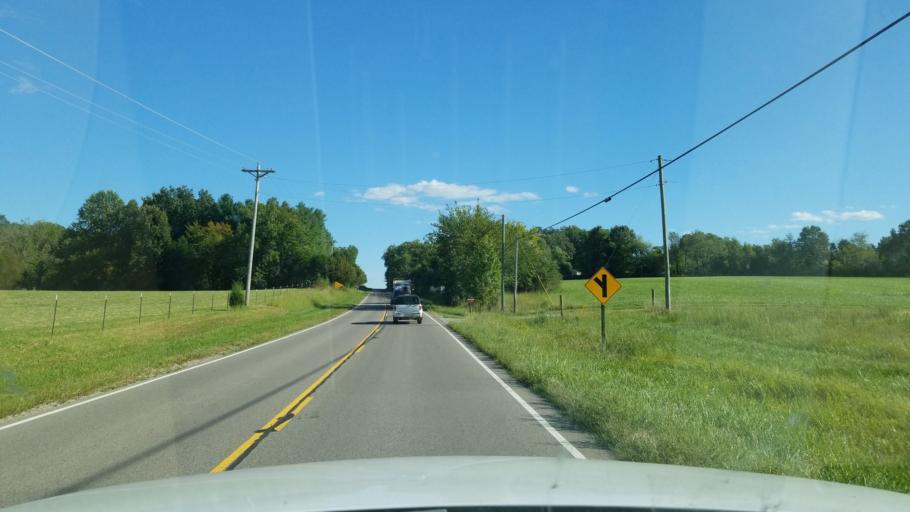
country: US
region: Illinois
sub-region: Saline County
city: Harrisburg
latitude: 37.6248
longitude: -88.4744
